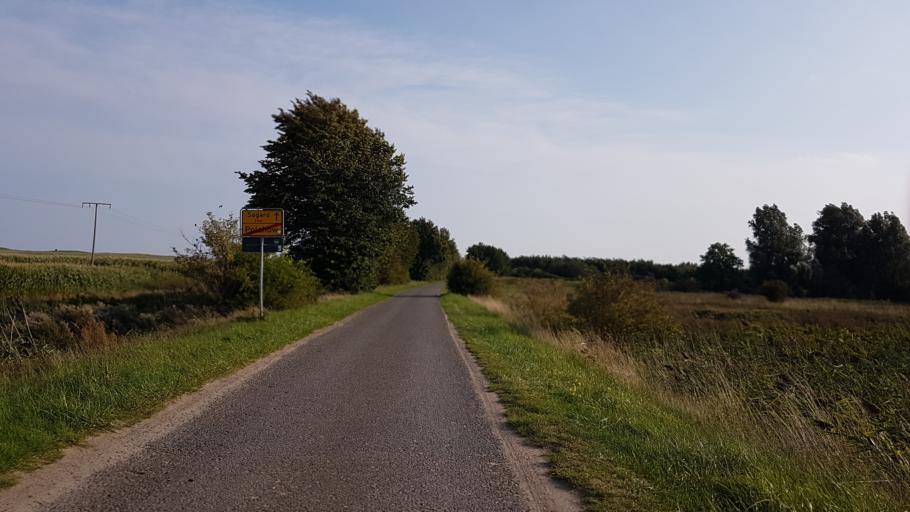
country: DE
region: Mecklenburg-Vorpommern
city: Sagard
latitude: 54.5413
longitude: 13.5089
